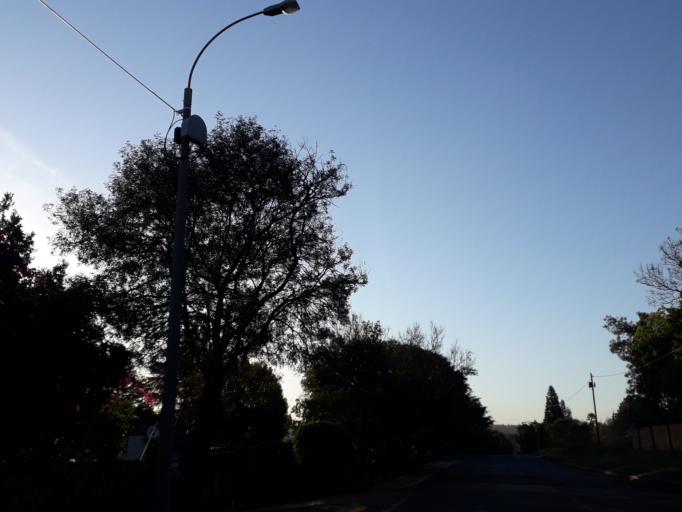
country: ZA
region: Gauteng
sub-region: City of Johannesburg Metropolitan Municipality
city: Roodepoort
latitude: -26.1610
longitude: 27.9393
